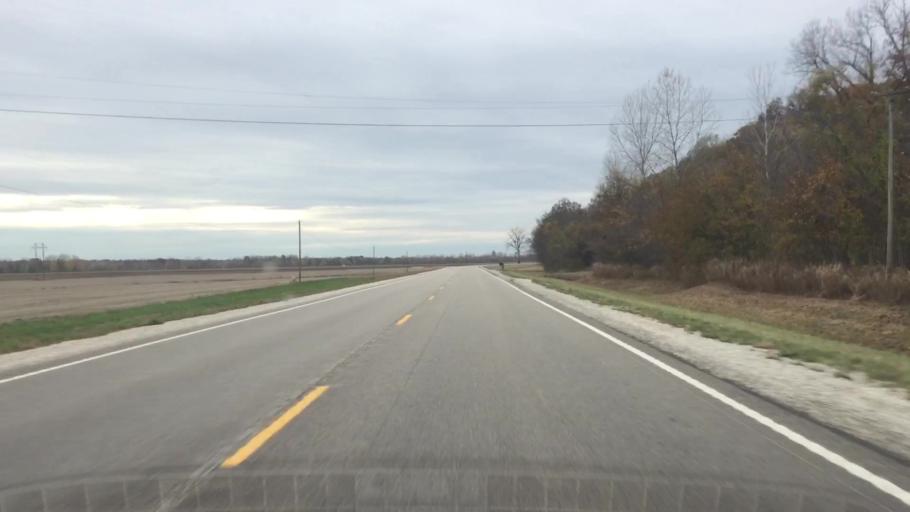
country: US
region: Missouri
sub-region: Callaway County
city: Holts Summit
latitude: 38.5805
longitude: -92.0915
